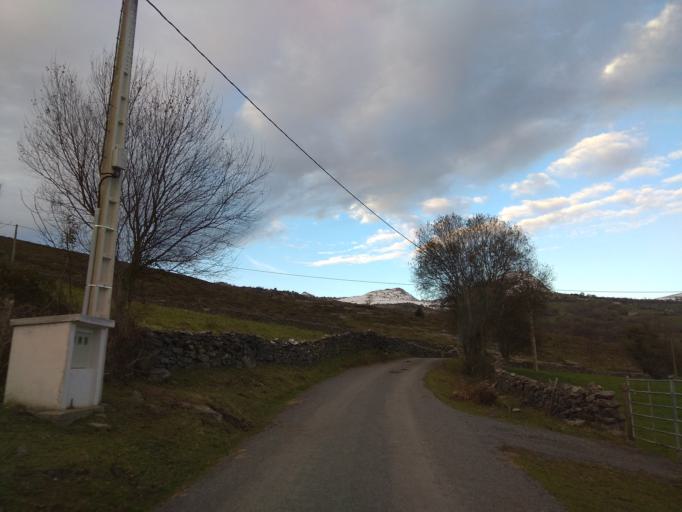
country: ES
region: Cantabria
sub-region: Provincia de Cantabria
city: Arredondo
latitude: 43.1961
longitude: -3.5774
